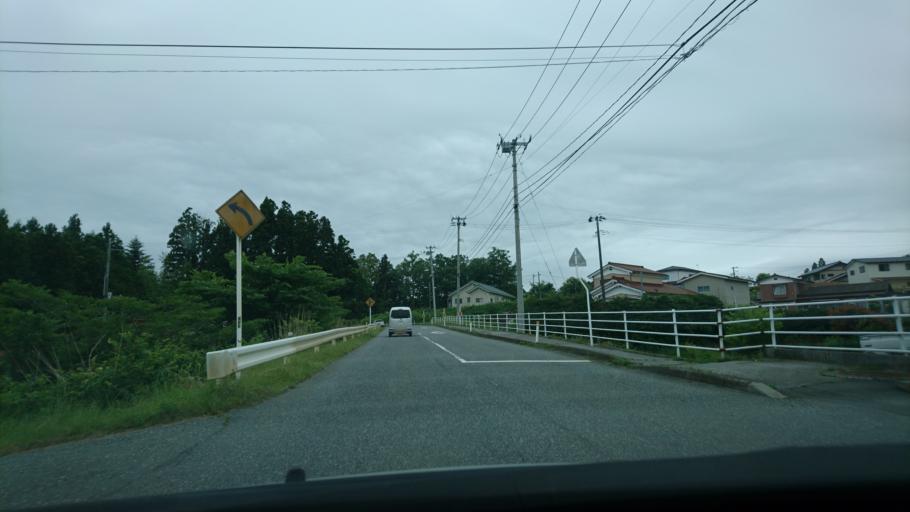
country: JP
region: Miyagi
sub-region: Oshika Gun
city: Onagawa Cho
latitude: 38.7861
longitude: 141.5086
